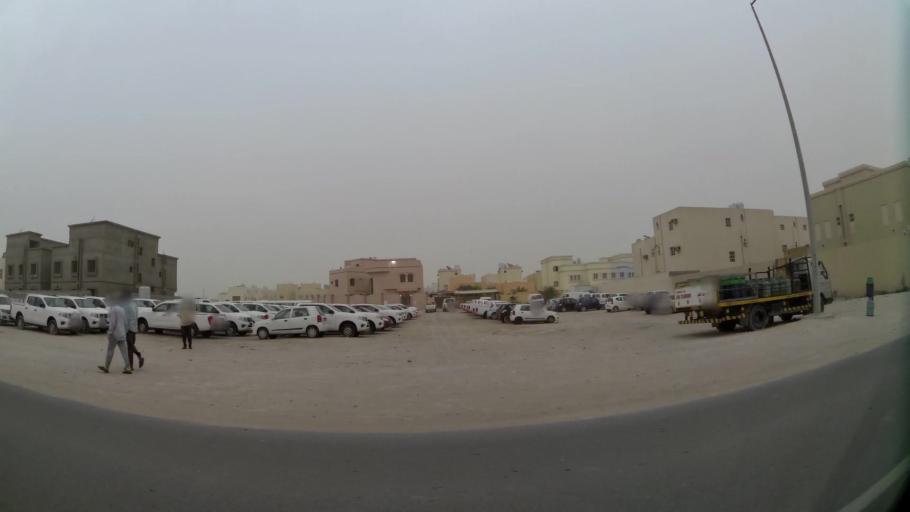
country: QA
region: Baladiyat ad Dawhah
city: Doha
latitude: 25.2432
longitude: 51.4812
